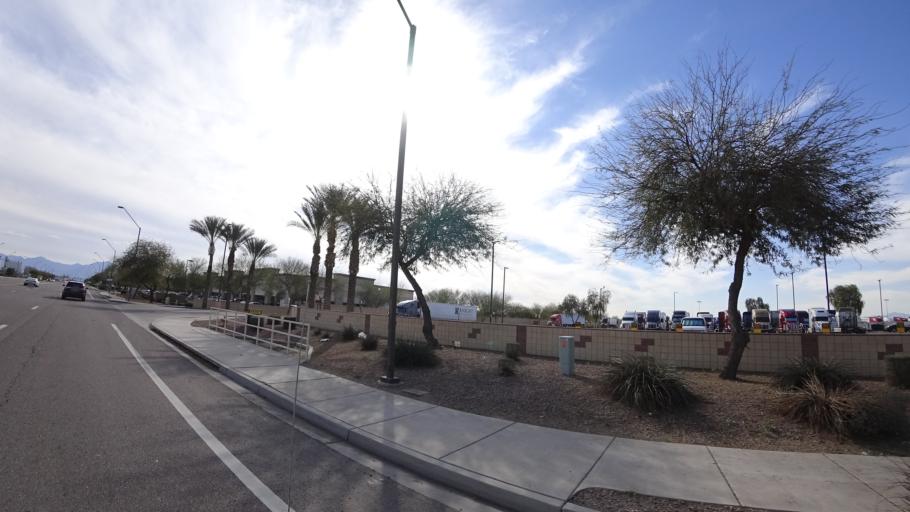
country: US
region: Arizona
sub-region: Maricopa County
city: Tolleson
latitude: 33.4560
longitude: -112.2727
